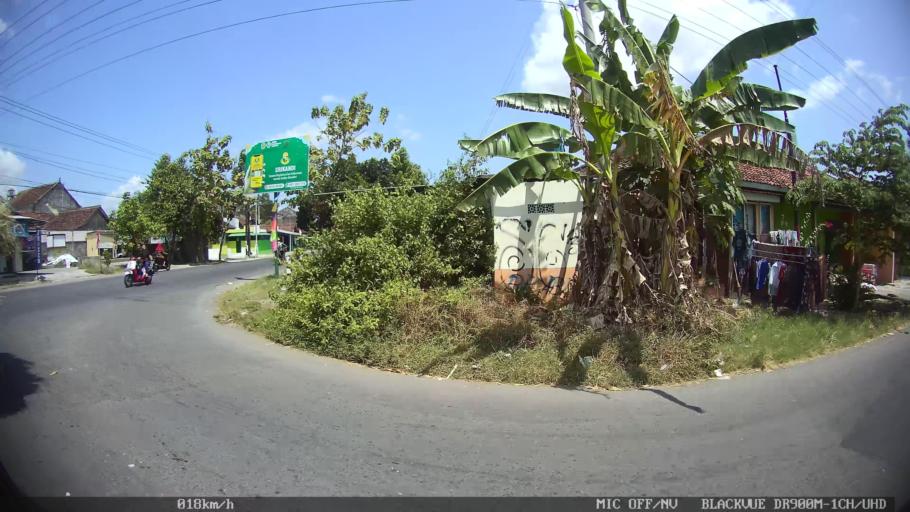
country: ID
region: Daerah Istimewa Yogyakarta
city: Sewon
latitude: -7.8987
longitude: 110.3842
